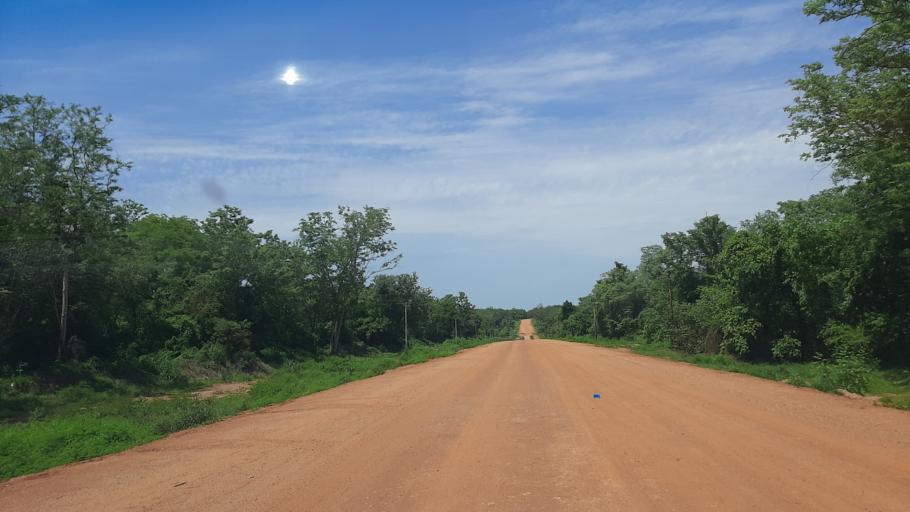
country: ET
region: Gambela
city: Gambela
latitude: 8.0936
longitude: 34.5886
